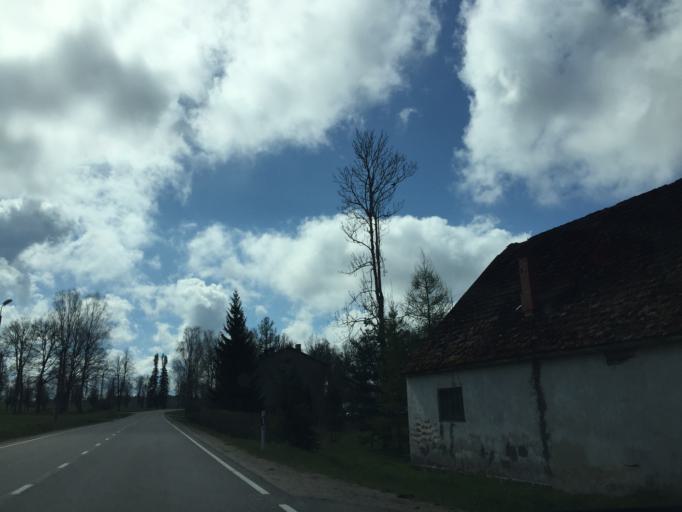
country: LV
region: Apes Novads
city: Ape
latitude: 57.5318
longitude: 26.6981
